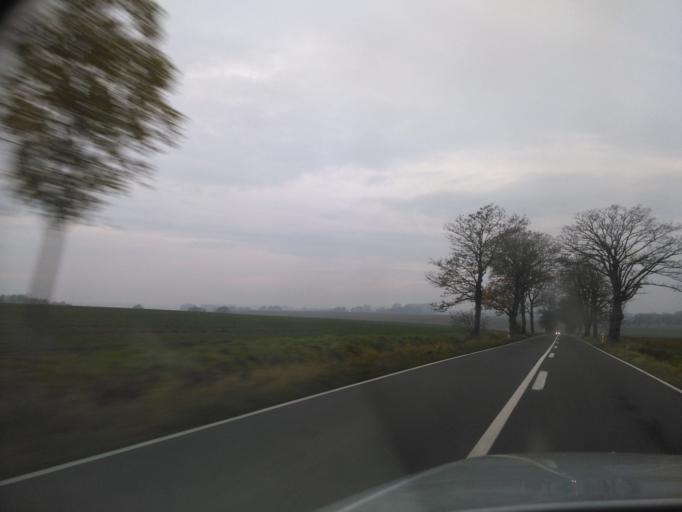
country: DE
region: Mecklenburg-Vorpommern
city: Rambin
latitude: 54.3099
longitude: 13.1810
